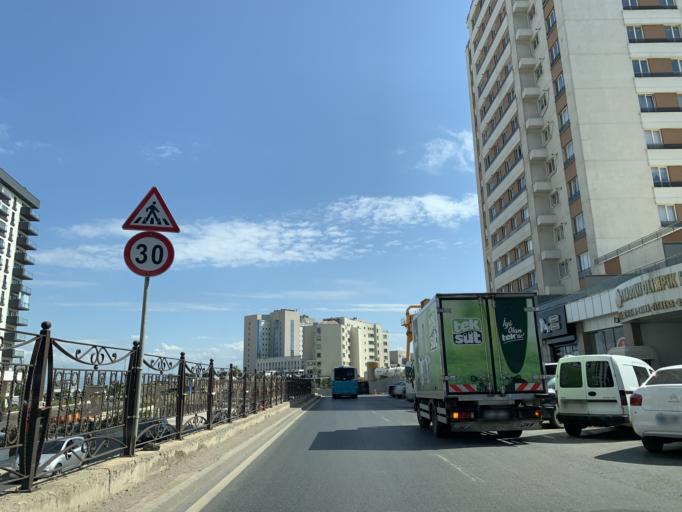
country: TR
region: Istanbul
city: Pendik
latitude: 40.8903
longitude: 29.2630
